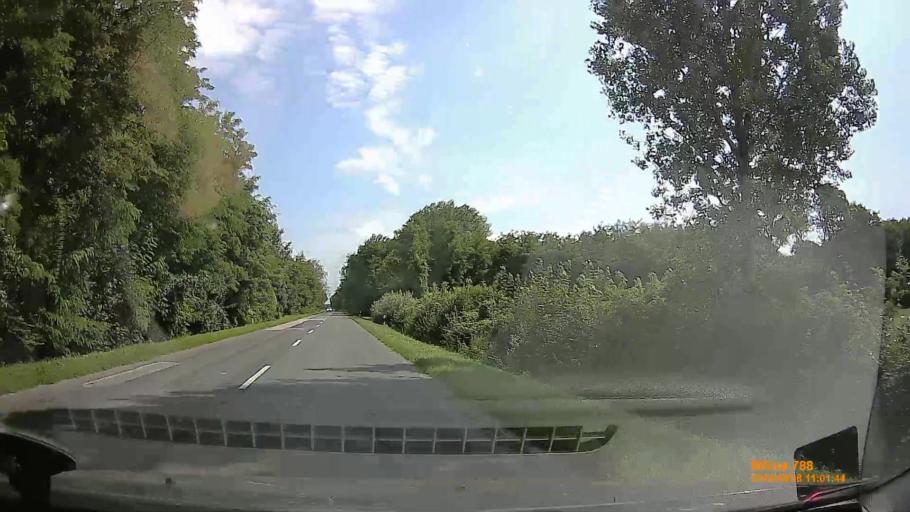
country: HU
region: Zala
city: Zalakomar
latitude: 46.5139
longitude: 17.1316
